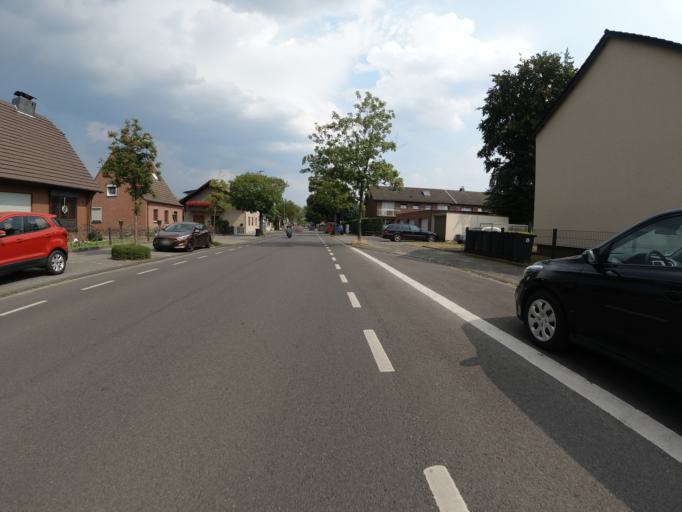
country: DE
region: North Rhine-Westphalia
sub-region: Regierungsbezirk Dusseldorf
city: Moers
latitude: 51.3922
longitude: 6.6461
